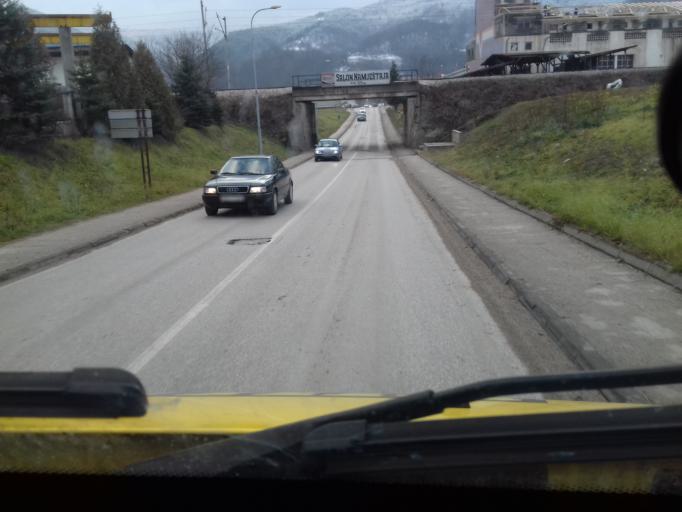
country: BA
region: Federation of Bosnia and Herzegovina
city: Zepce
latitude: 44.4295
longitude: 18.0404
